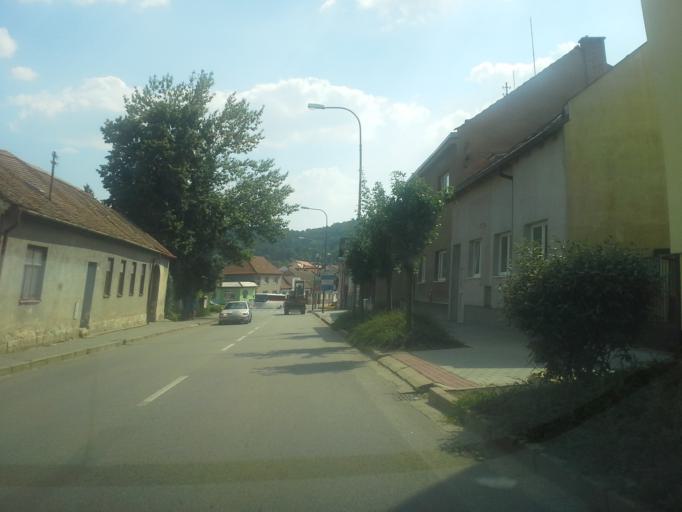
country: CZ
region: South Moravian
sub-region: Okres Blansko
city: Boskovice
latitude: 49.4914
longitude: 16.6626
